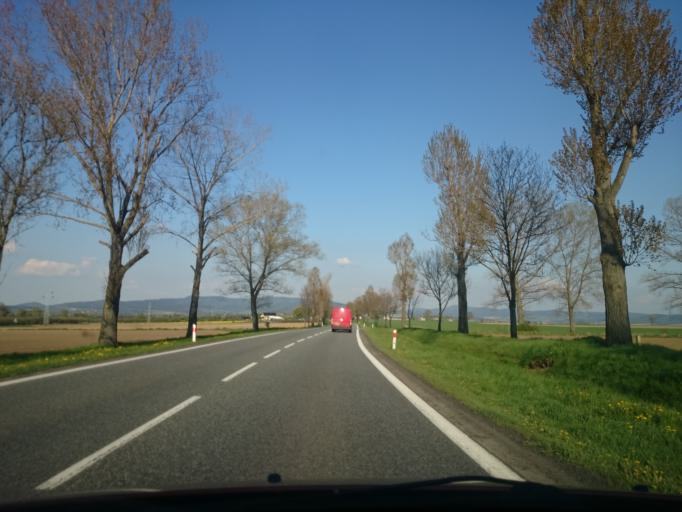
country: PL
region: Lower Silesian Voivodeship
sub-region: Powiat klodzki
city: Klodzko
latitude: 50.4372
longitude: 16.5967
